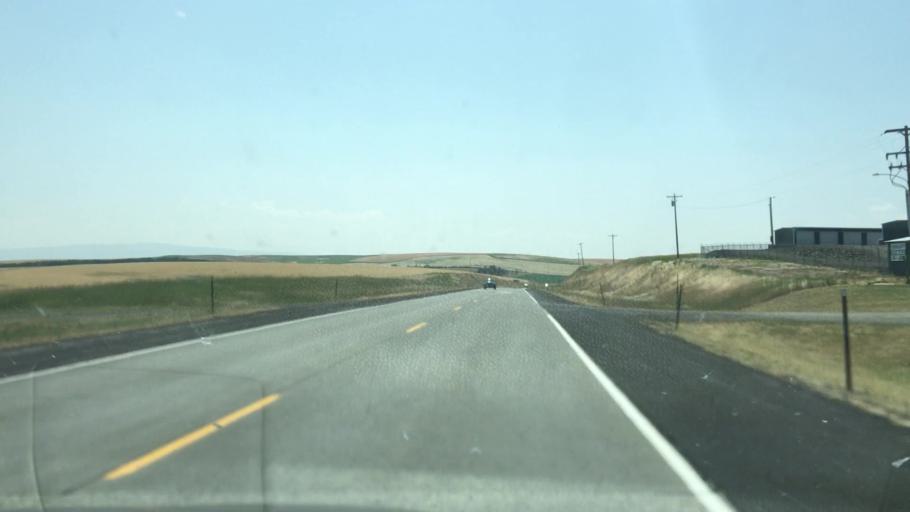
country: US
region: Idaho
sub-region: Lewis County
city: Nezperce
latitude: 46.0772
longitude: -116.3433
